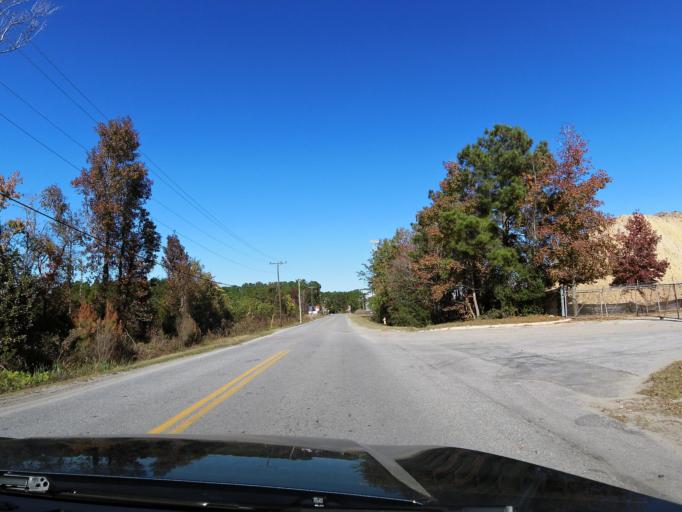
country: US
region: Georgia
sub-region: Chatham County
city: Savannah
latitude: 32.0654
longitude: -81.1440
